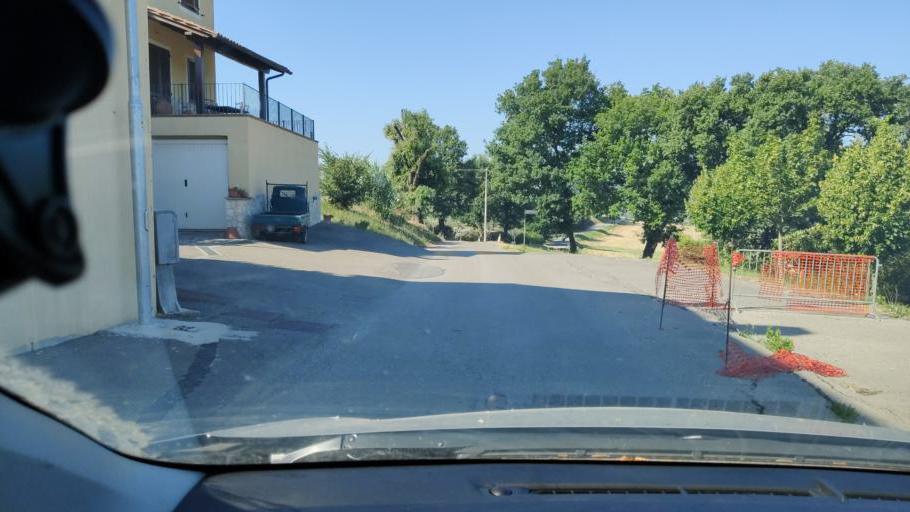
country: IT
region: Umbria
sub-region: Provincia di Terni
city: Amelia
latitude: 42.5144
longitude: 12.4275
